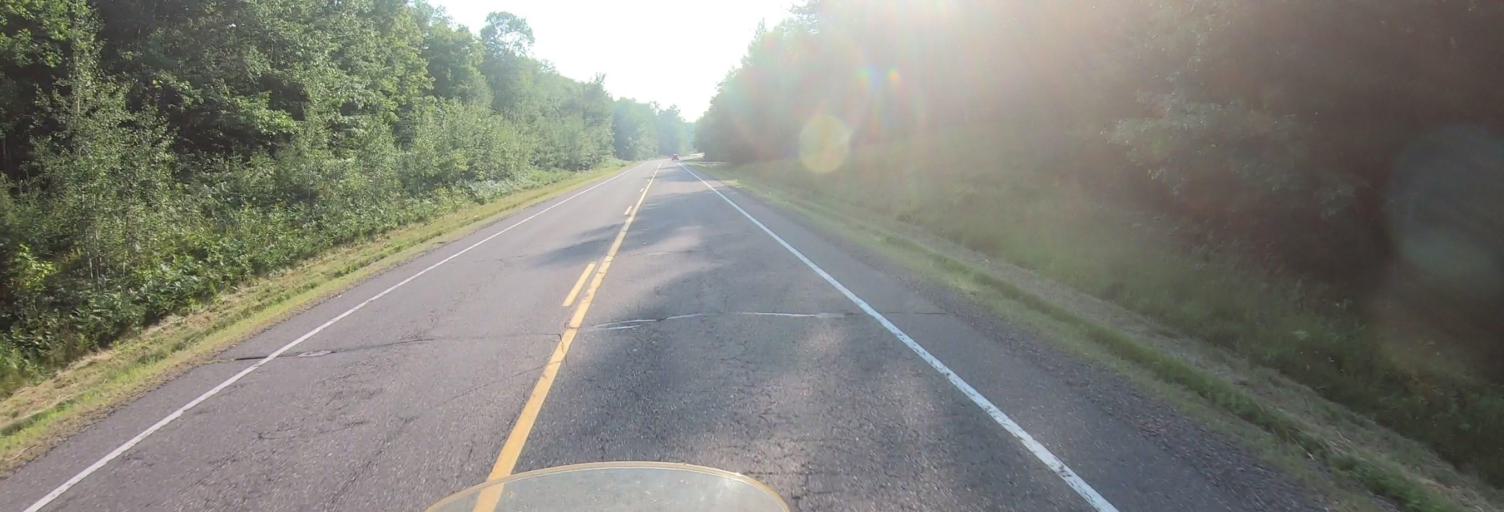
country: US
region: Wisconsin
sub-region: Sawyer County
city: Little Round Lake
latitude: 46.0724
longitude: -91.0884
